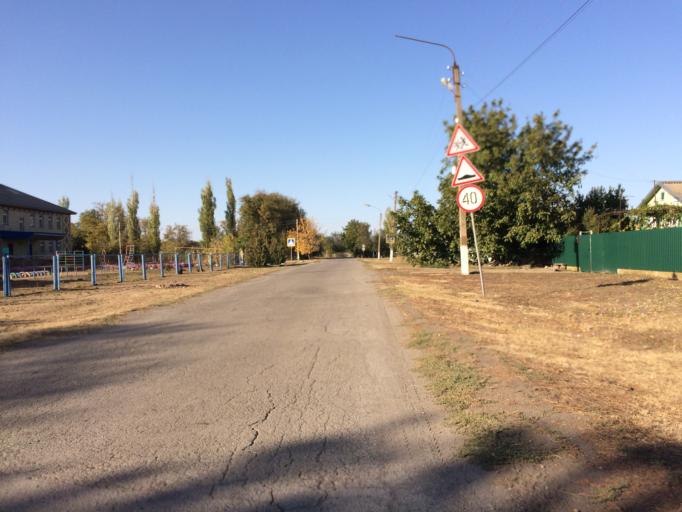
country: RU
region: Rostov
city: Tselina
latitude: 46.5173
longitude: 41.1840
